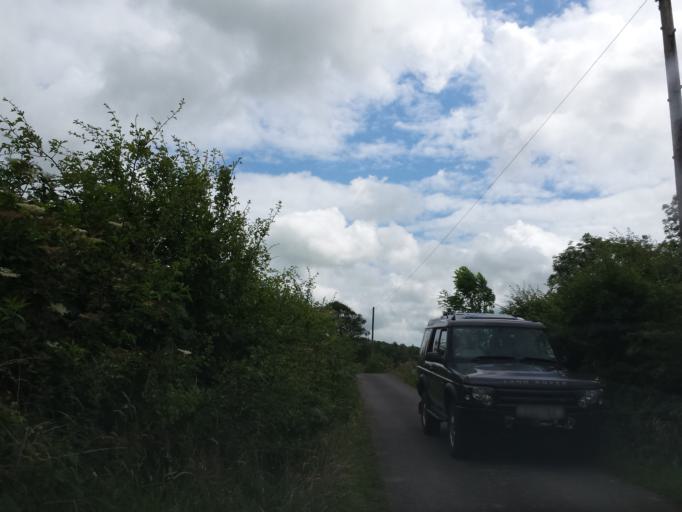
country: GB
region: Scotland
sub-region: Dumfries and Galloway
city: Castle Douglas
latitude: 54.9325
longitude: -3.9568
